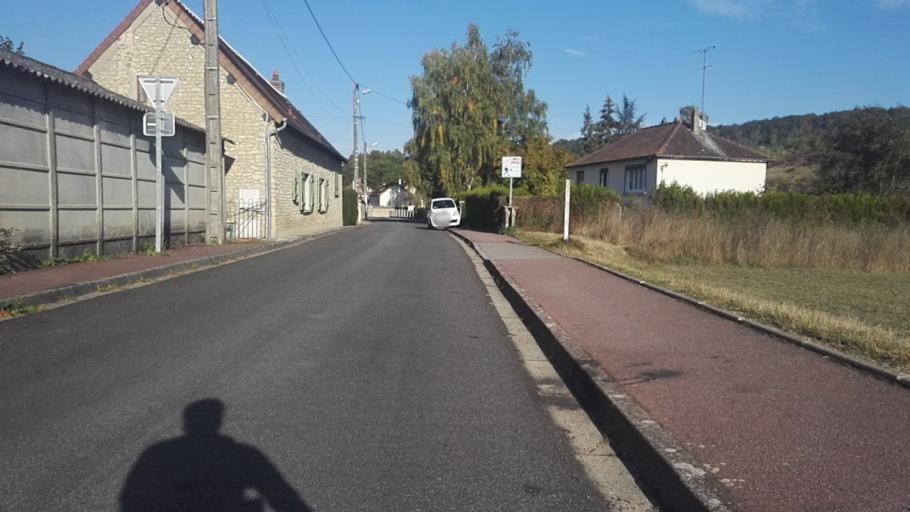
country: FR
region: Haute-Normandie
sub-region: Departement de l'Eure
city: Menilles
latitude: 49.0346
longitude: 1.3613
